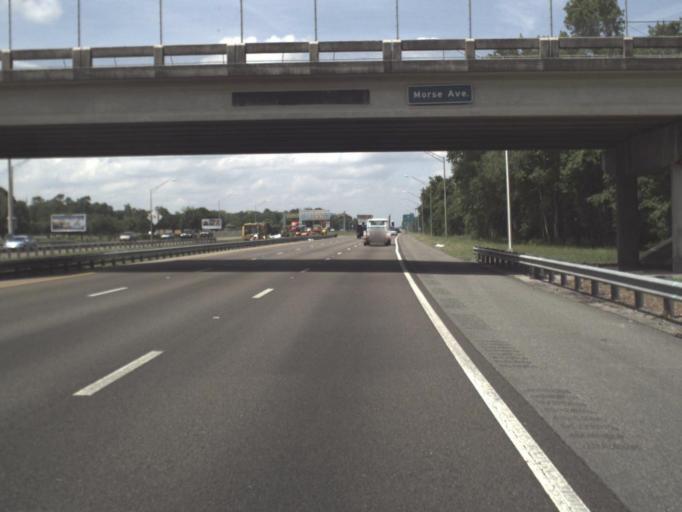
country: US
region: Florida
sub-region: Clay County
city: Bellair-Meadowbrook Terrace
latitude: 30.2257
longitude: -81.7626
